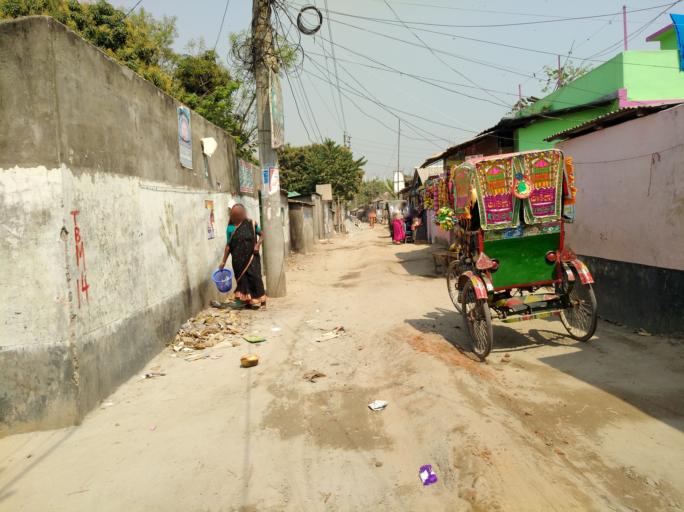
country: BD
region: Dhaka
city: Tungi
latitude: 23.9220
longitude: 90.4004
